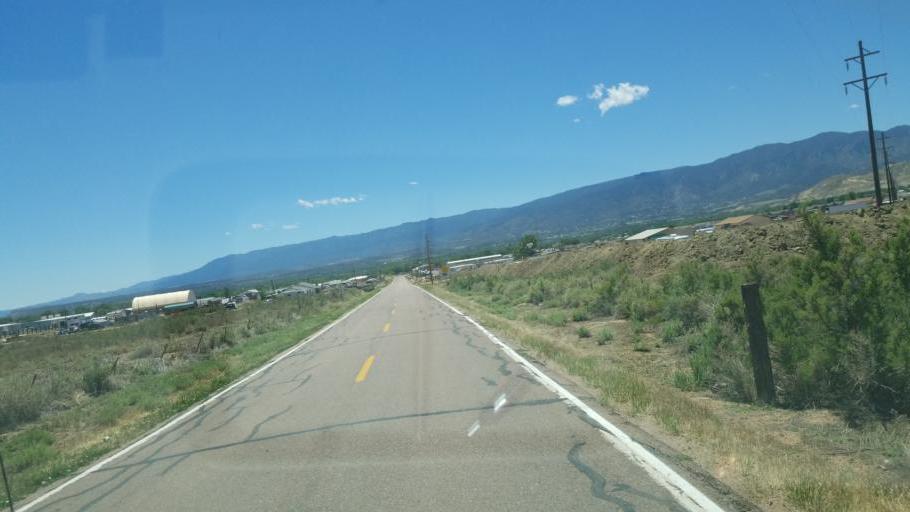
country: US
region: Colorado
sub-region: Fremont County
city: Canon City
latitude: 38.4773
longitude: -105.2226
